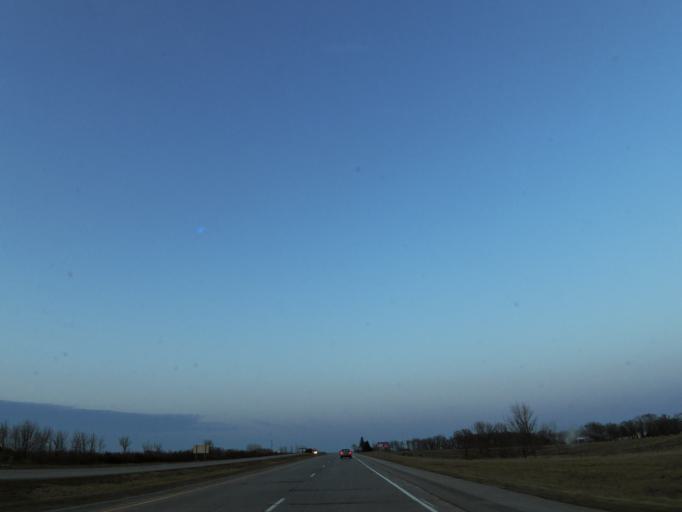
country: US
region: Minnesota
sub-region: Mower County
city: Grand Meadow
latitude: 43.7000
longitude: -92.7169
